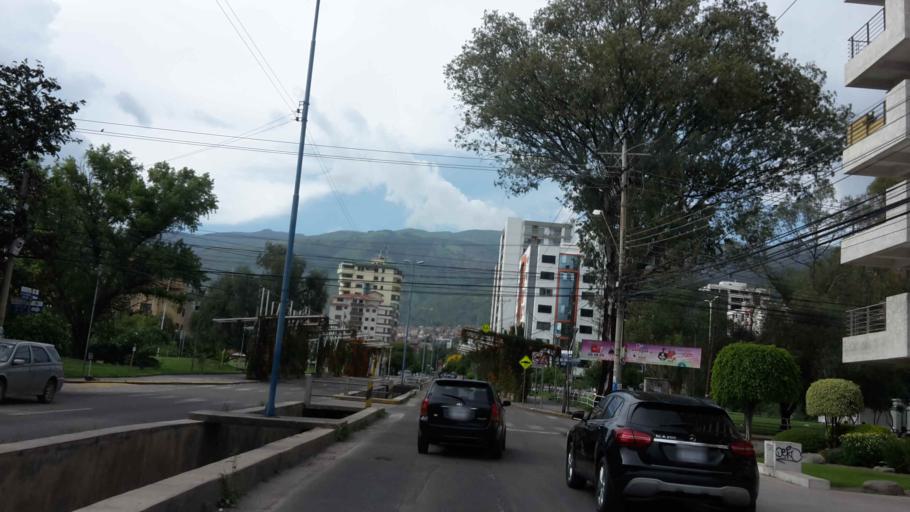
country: BO
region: Cochabamba
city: Cochabamba
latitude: -17.3757
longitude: -66.1592
